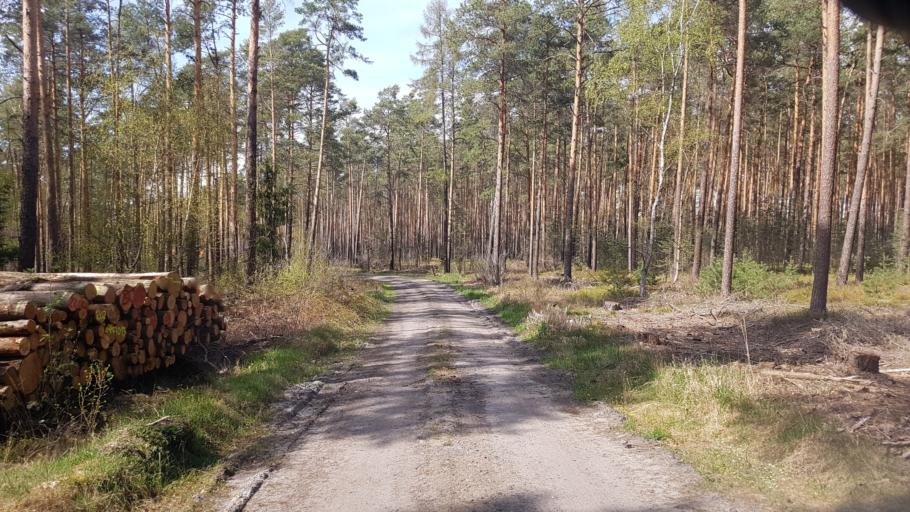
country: DE
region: Brandenburg
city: Plessa
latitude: 51.5483
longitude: 13.6519
